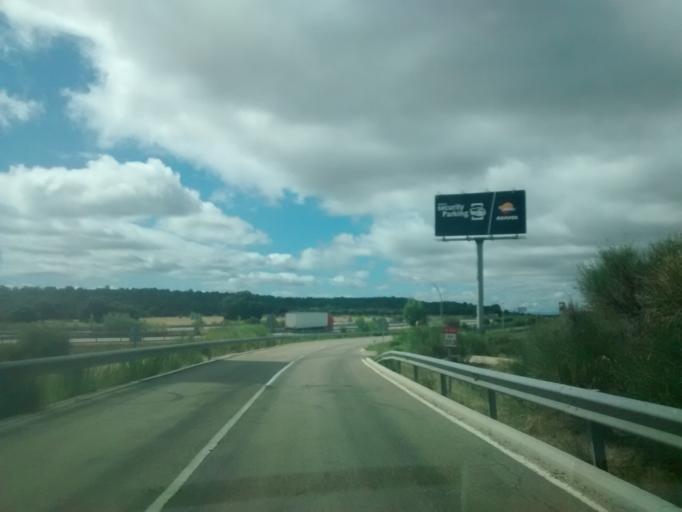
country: ES
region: Castille and Leon
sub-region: Provincia de Salamanca
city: Tenebron
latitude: 40.6662
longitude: -6.4358
